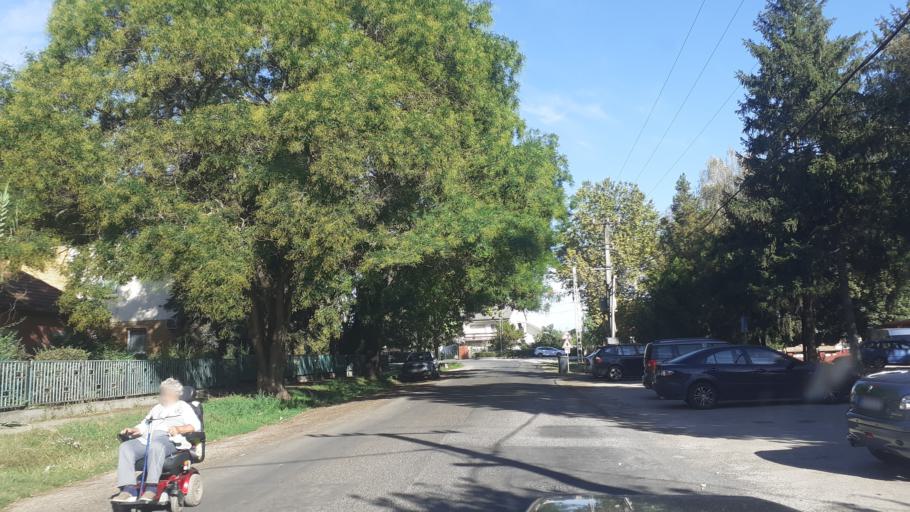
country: HU
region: Fejer
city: Ivancsa
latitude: 47.1907
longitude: 18.7946
